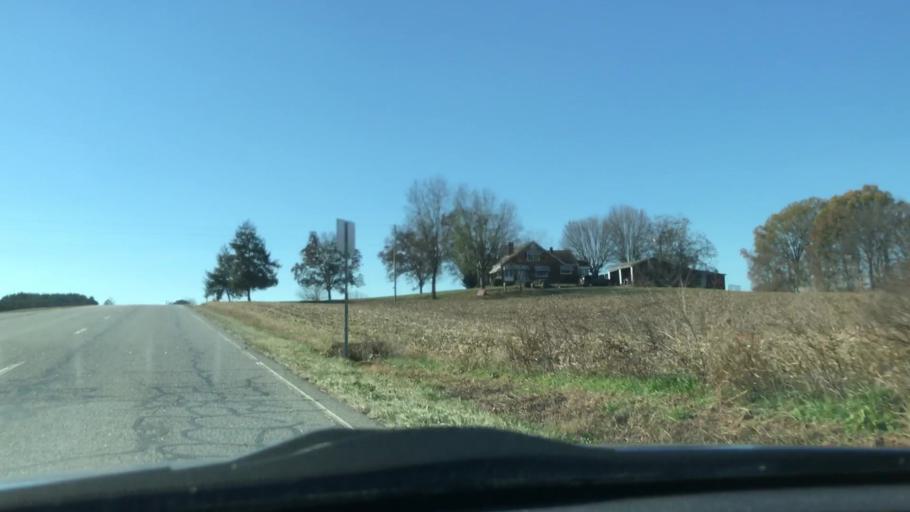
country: US
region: North Carolina
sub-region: Davidson County
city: Denton
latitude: 35.5899
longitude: -80.0488
